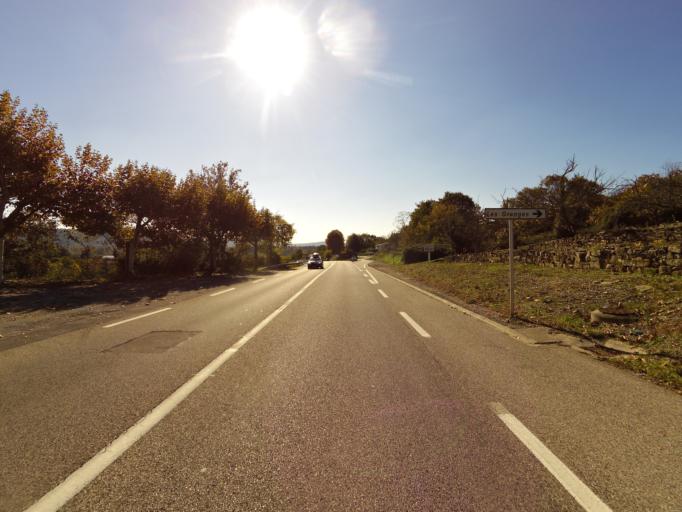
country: FR
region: Rhone-Alpes
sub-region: Departement de l'Ardeche
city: Saint-Privat
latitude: 44.6320
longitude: 4.4216
